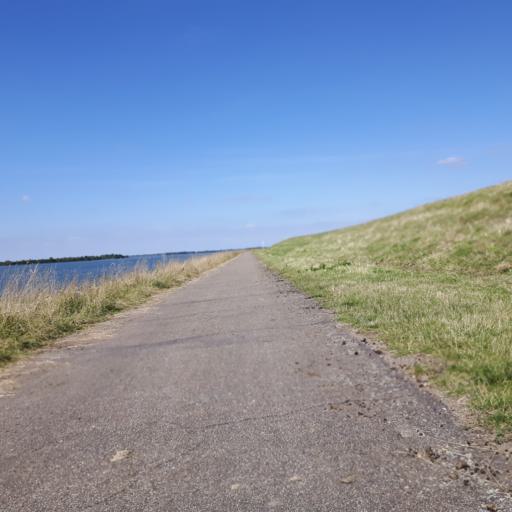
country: NL
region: Zeeland
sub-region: Gemeente Tholen
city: Tholen
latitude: 51.4781
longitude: 4.2281
